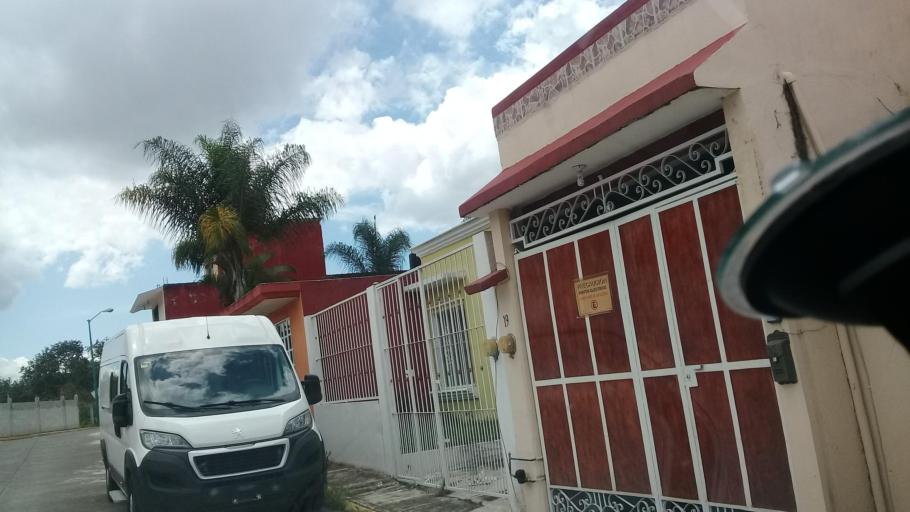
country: MX
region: Veracruz
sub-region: Xalapa
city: Lomas Verdes
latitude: 19.5012
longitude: -96.8908
